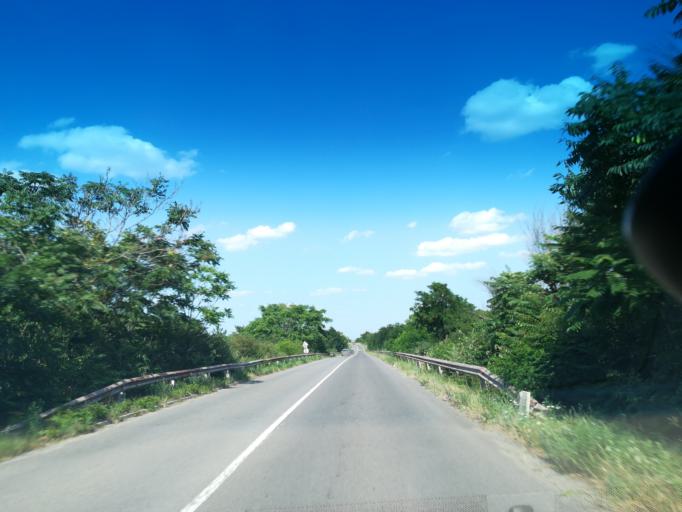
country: BG
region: Stara Zagora
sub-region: Obshtina Chirpan
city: Chirpan
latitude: 42.2180
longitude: 25.3770
